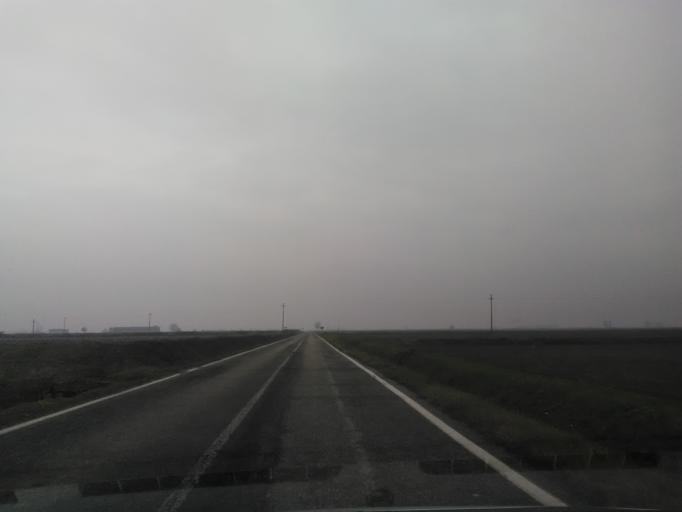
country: IT
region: Piedmont
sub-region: Provincia di Vercelli
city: Salasco
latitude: 45.3004
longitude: 8.2661
